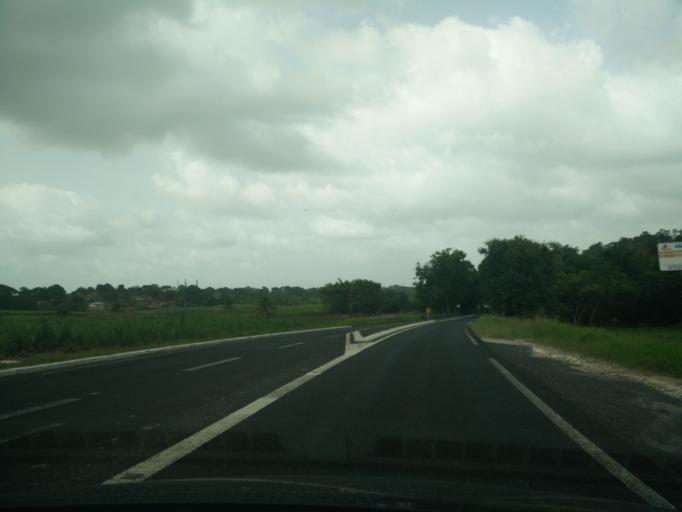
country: GP
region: Guadeloupe
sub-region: Guadeloupe
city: Petit-Bourg
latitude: 16.2142
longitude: -61.6218
